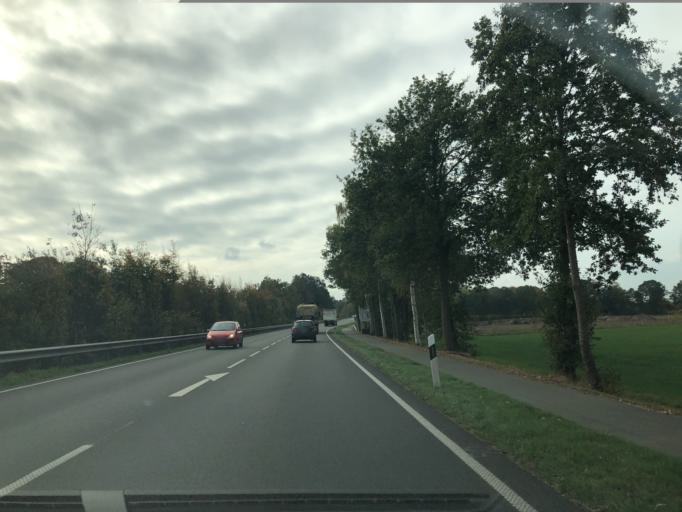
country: DE
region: Lower Saxony
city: Friesoythe
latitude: 53.0600
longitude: 7.8060
